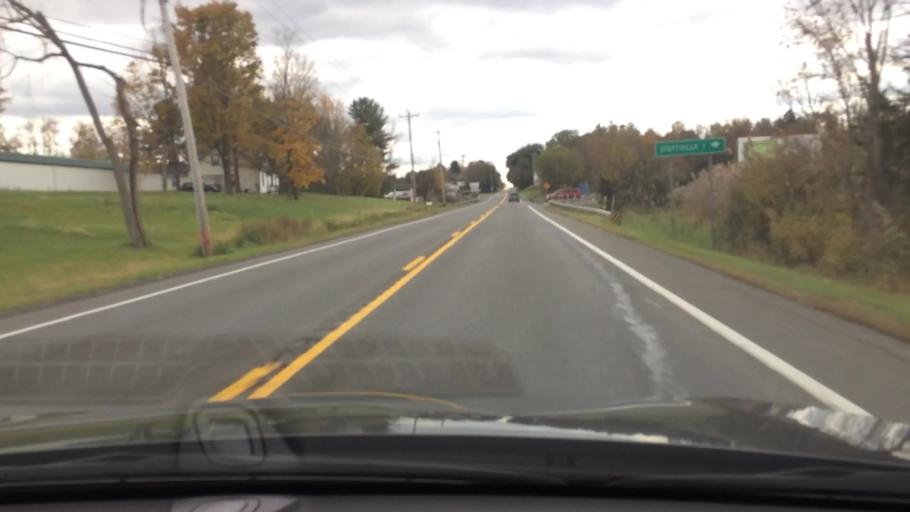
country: US
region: New York
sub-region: Columbia County
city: Stottville
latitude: 42.2885
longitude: -73.7167
